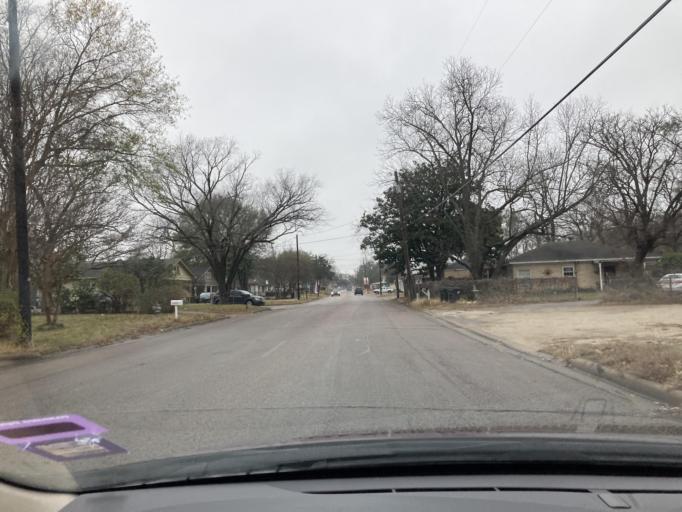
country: US
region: Texas
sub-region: Navarro County
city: Corsicana
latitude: 32.1018
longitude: -96.4695
